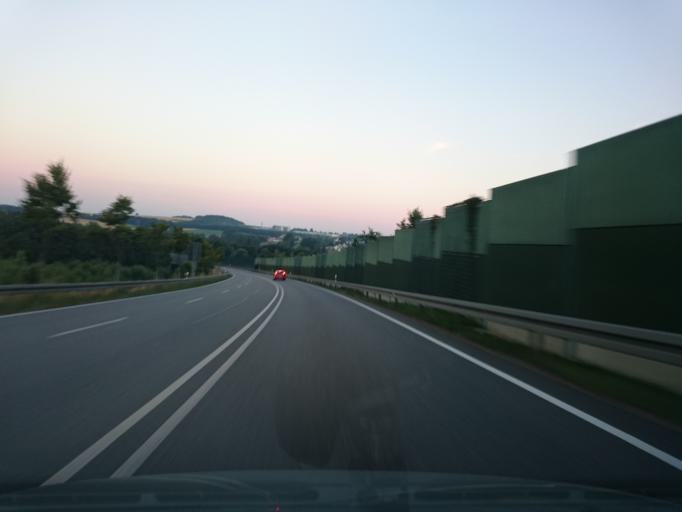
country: DE
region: Saxony
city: Stollberg
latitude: 50.6979
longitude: 12.7807
